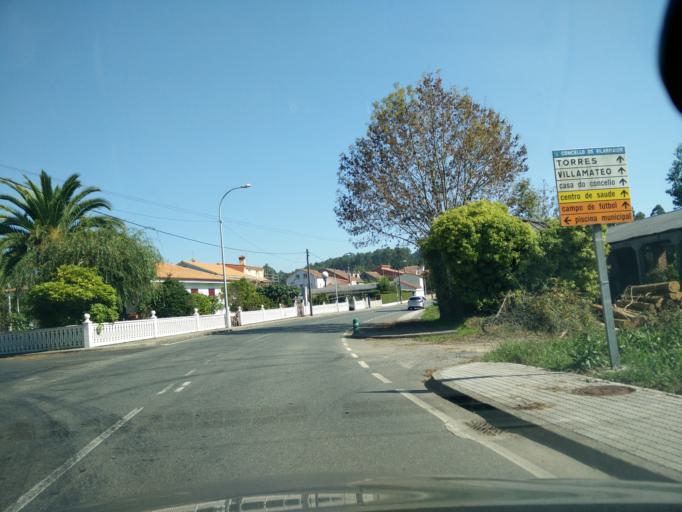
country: ES
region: Galicia
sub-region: Provincia da Coruna
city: Mino
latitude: 43.3401
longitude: -8.1576
